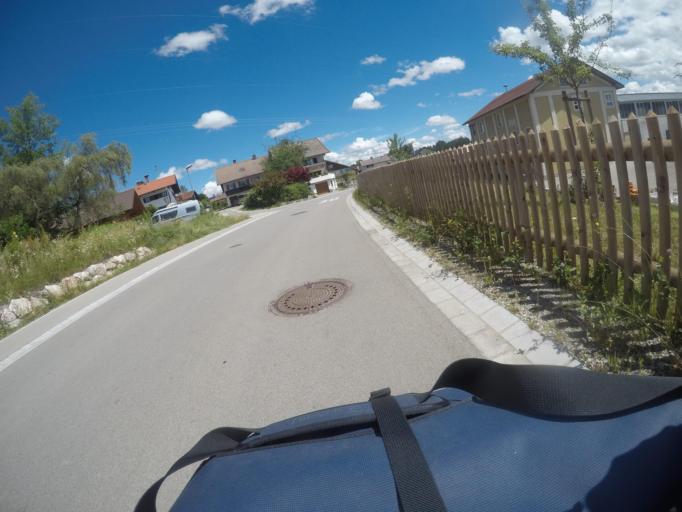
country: DE
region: Bavaria
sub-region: Swabia
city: Lechbruck
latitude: 47.6928
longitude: 10.7965
